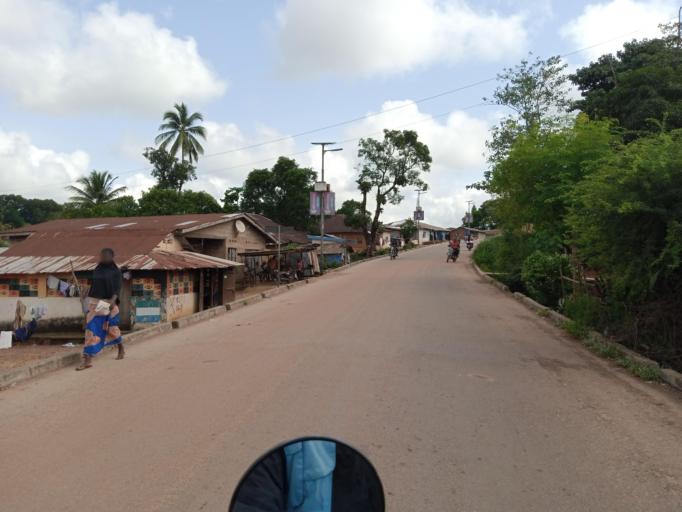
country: SL
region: Southern Province
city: Bo
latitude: 7.9754
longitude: -11.7391
